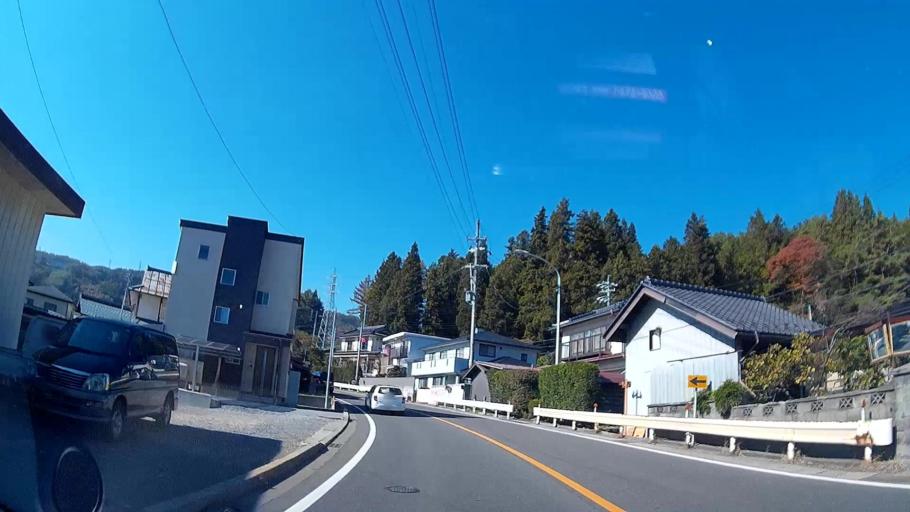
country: JP
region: Nagano
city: Okaya
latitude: 36.0849
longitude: 138.0429
